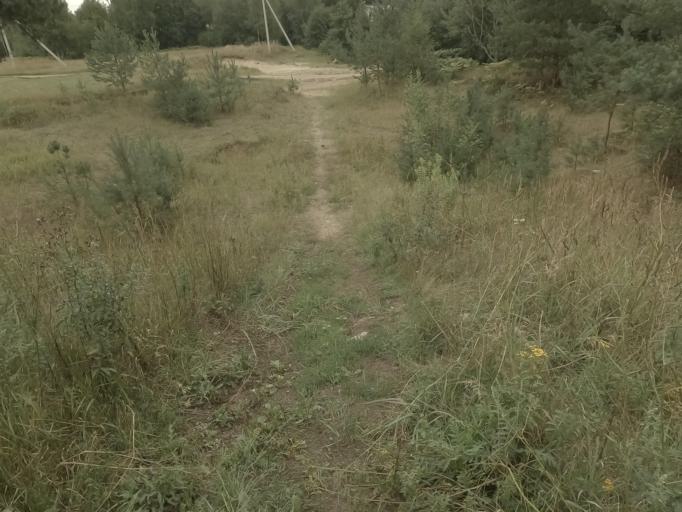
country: RU
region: Leningrad
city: Kirovsk
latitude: 59.8983
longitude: 31.0055
